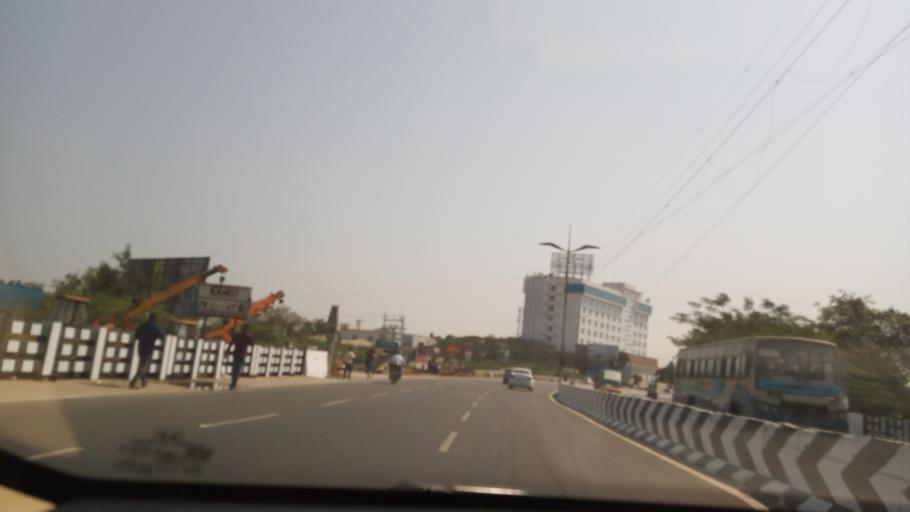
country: IN
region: Tamil Nadu
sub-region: Coimbatore
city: Irugur
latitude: 11.0571
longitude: 77.0682
